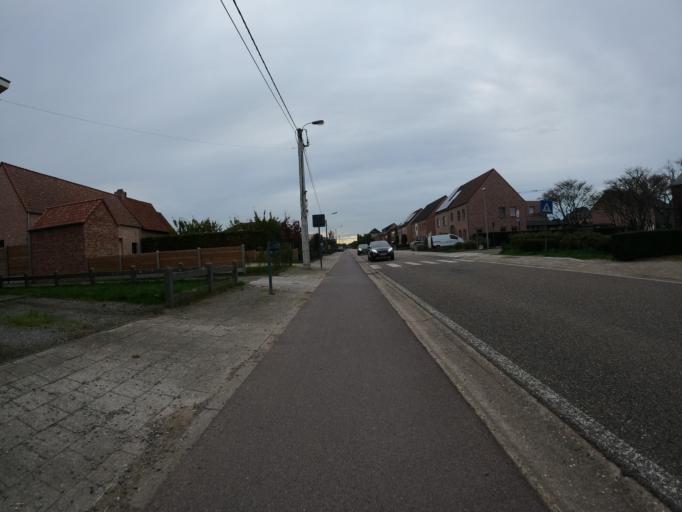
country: BE
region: Flanders
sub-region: Provincie Antwerpen
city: Herenthout
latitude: 51.1332
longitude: 4.7557
